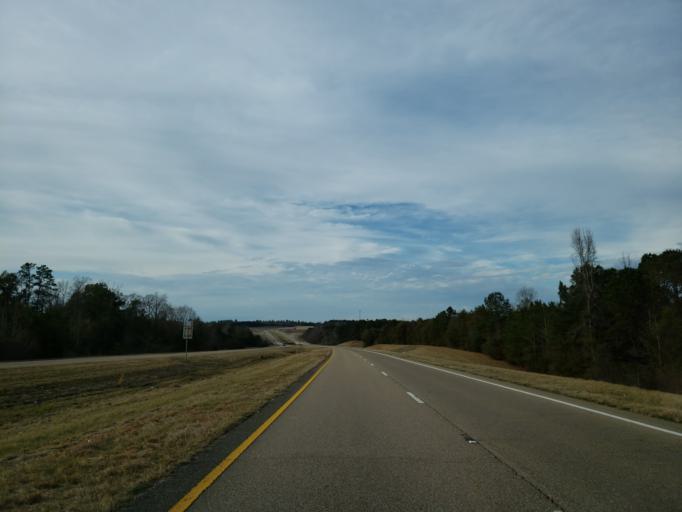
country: US
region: Mississippi
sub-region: Wayne County
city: Waynesboro
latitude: 31.6707
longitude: -88.6066
